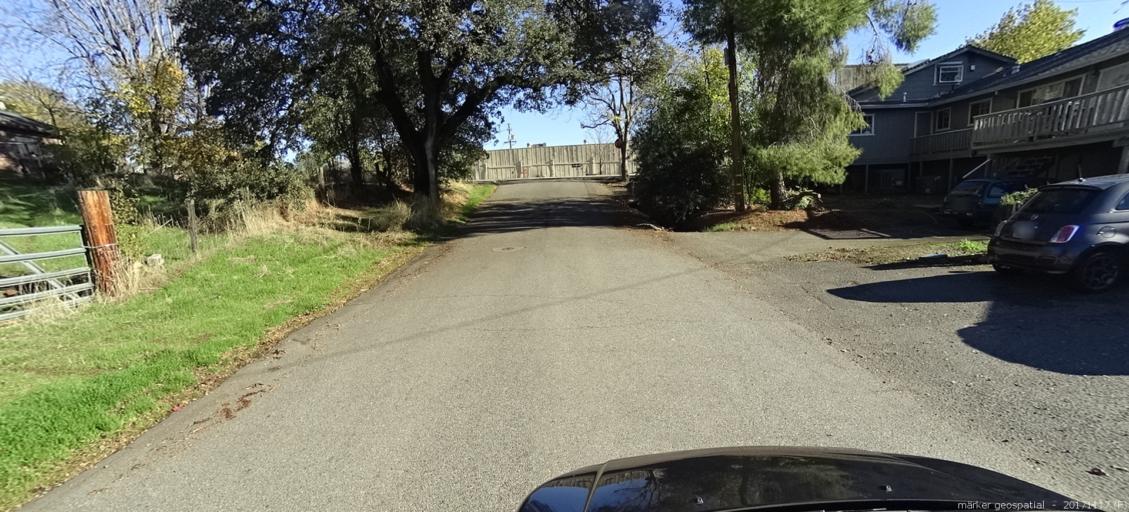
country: US
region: California
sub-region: Shasta County
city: Cottonwood
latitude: 40.3833
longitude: -122.2830
